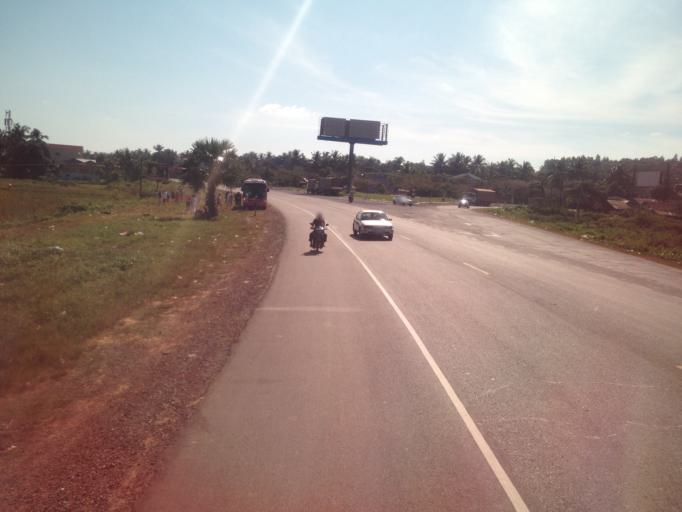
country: KH
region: Preah Sihanouk
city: Sihanoukville
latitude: 10.5861
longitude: 103.6436
